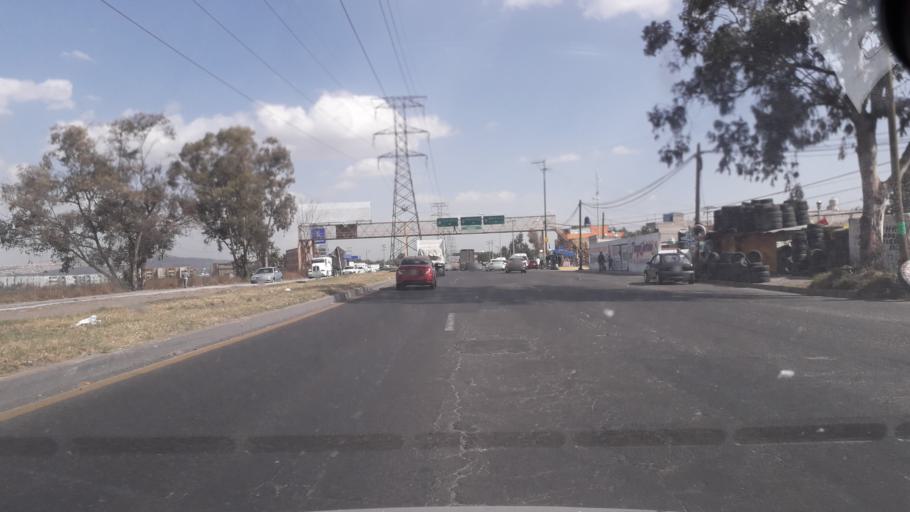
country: MX
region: Mexico
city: Ecatepec
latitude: 19.6141
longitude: -99.0382
